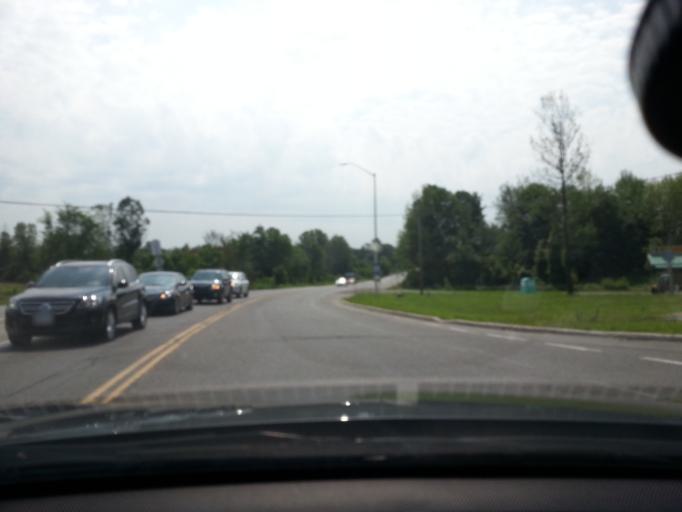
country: CA
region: Ontario
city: Bells Corners
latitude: 45.2469
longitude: -75.7112
